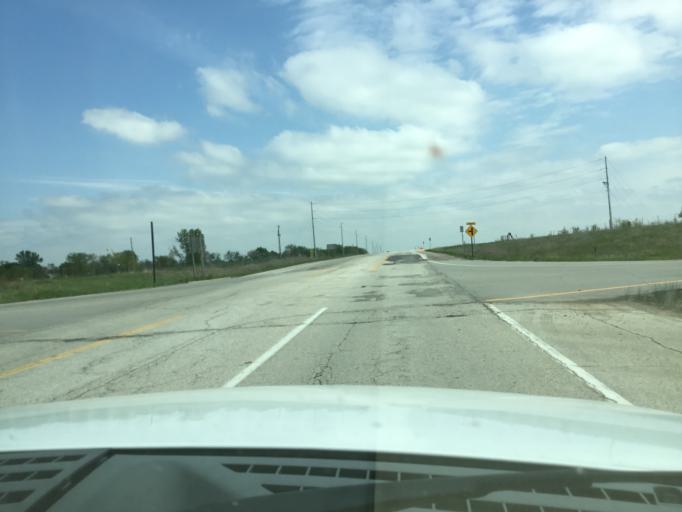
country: US
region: Kansas
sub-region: Shawnee County
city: Auburn
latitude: 38.9291
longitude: -95.7076
